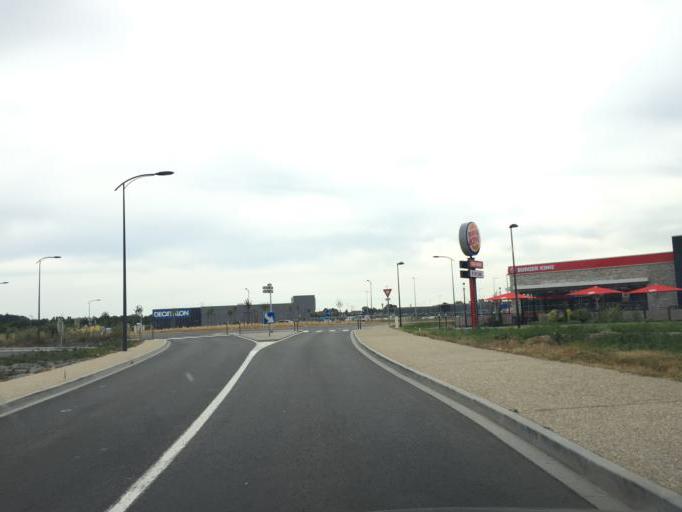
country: FR
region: Auvergne
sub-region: Departement de l'Allier
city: Avermes
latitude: 46.5903
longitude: 3.3229
